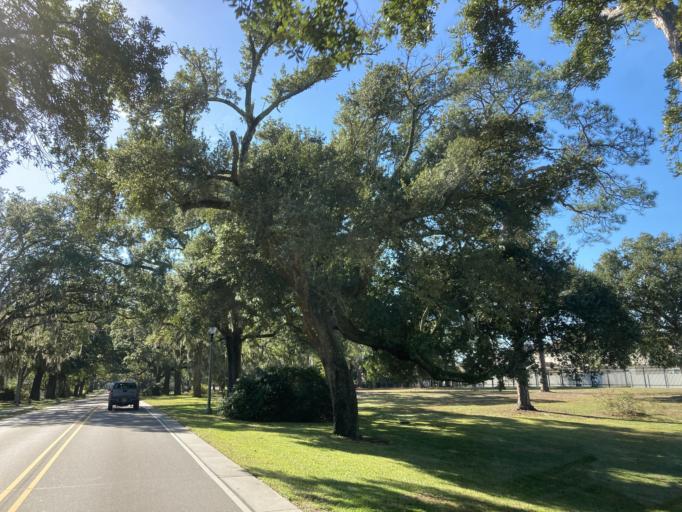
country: US
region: Mississippi
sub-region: Harrison County
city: D'Iberville
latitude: 30.4082
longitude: -88.9472
